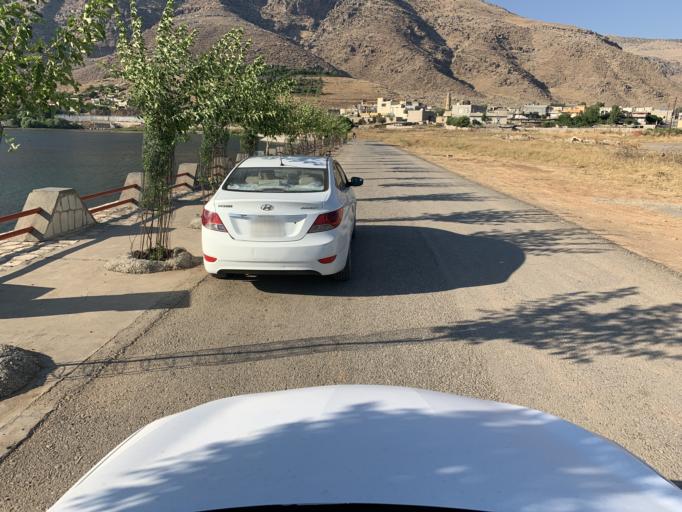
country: IQ
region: As Sulaymaniyah
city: Raniye
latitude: 36.2717
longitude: 44.7550
